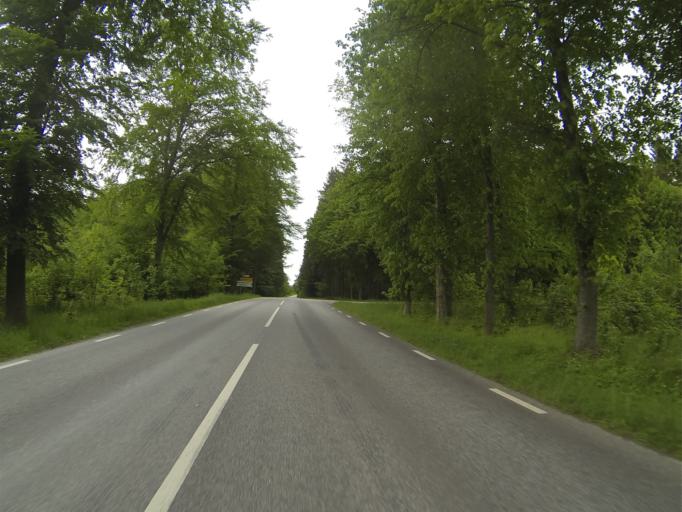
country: SE
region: Skane
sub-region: Sjobo Kommun
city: Sjoebo
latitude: 55.6659
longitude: 13.6724
